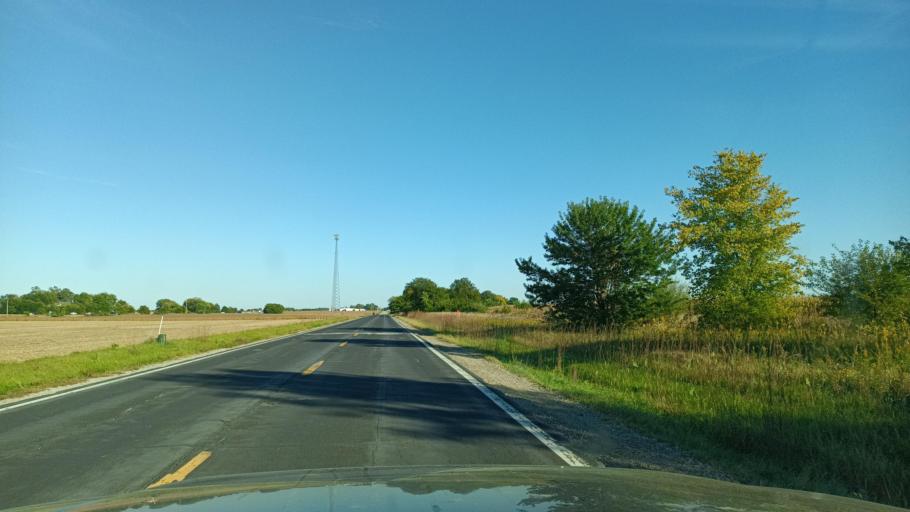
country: US
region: Illinois
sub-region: De Witt County
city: Farmer City
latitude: 40.2386
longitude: -88.6152
